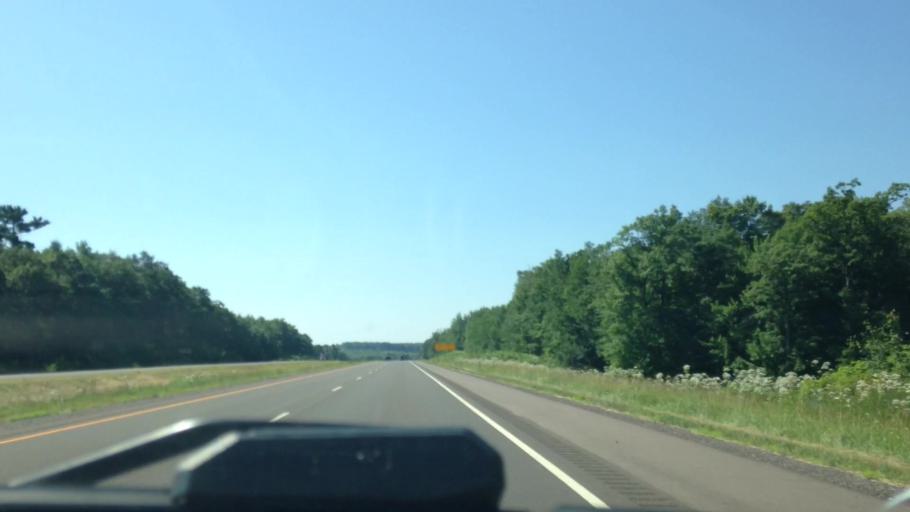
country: US
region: Wisconsin
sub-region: Washburn County
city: Spooner
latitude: 45.9898
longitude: -91.8297
